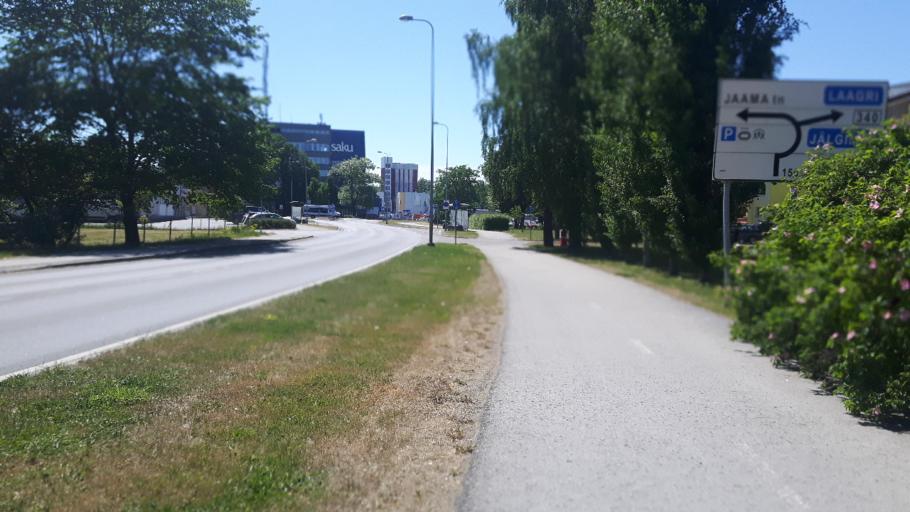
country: EE
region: Harju
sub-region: Saku vald
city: Saku
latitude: 59.3031
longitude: 24.6689
